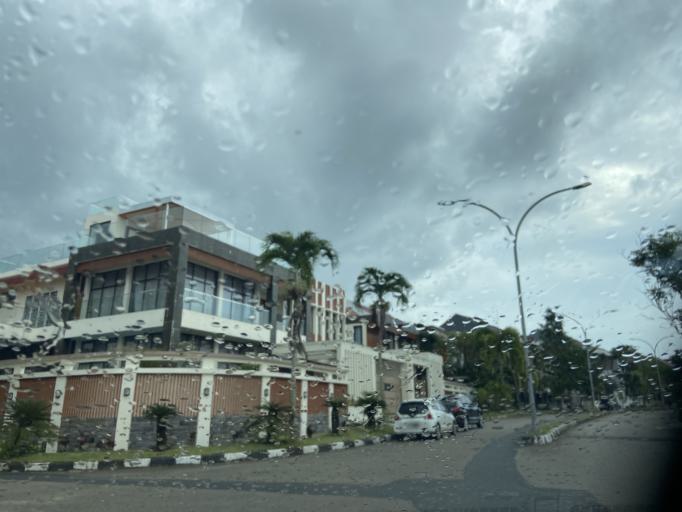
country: SG
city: Singapore
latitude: 1.1044
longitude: 104.0259
